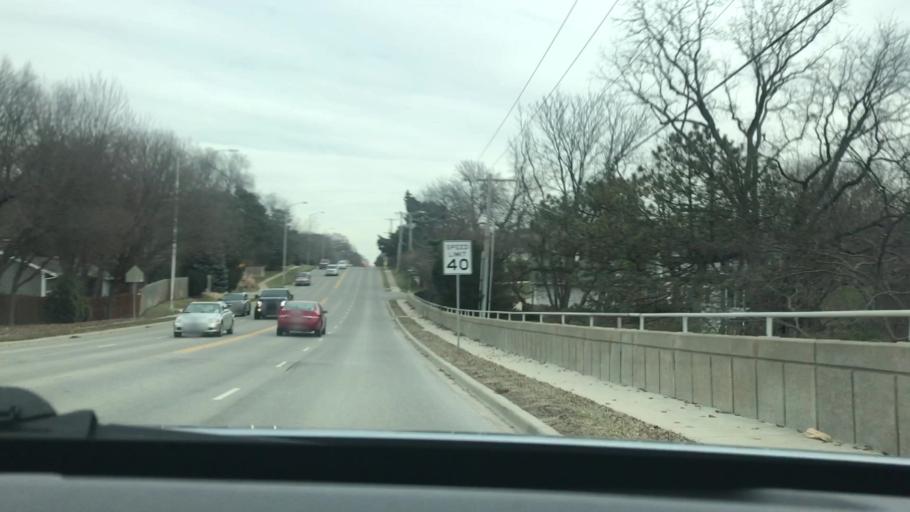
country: US
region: Kansas
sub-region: Johnson County
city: Leawood
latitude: 38.9422
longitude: -94.6346
